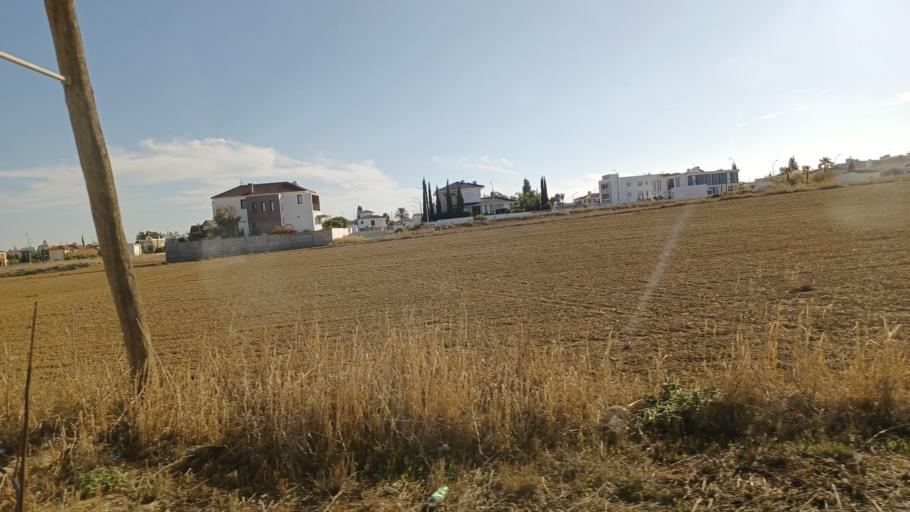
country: CY
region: Larnaka
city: Athienou
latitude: 35.0568
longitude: 33.5381
